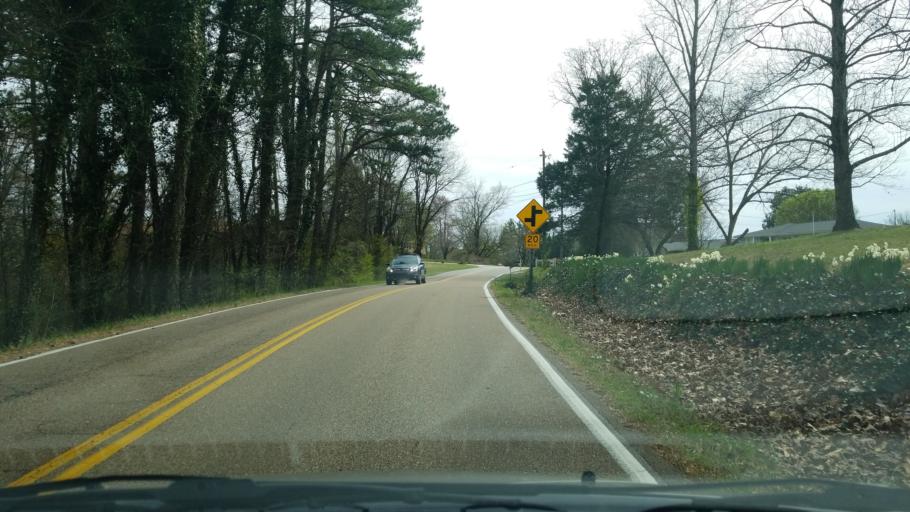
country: US
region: Tennessee
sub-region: Hamilton County
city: East Brainerd
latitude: 35.0173
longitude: -85.1200
